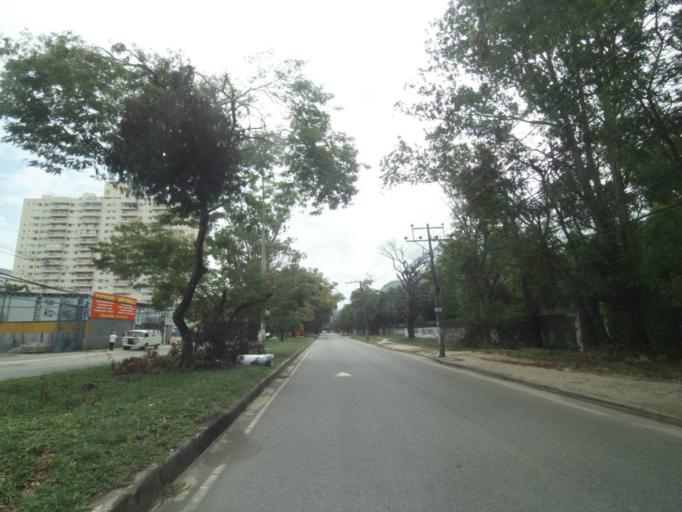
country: BR
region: Rio de Janeiro
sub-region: Nilopolis
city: Nilopolis
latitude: -22.9626
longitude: -43.4006
